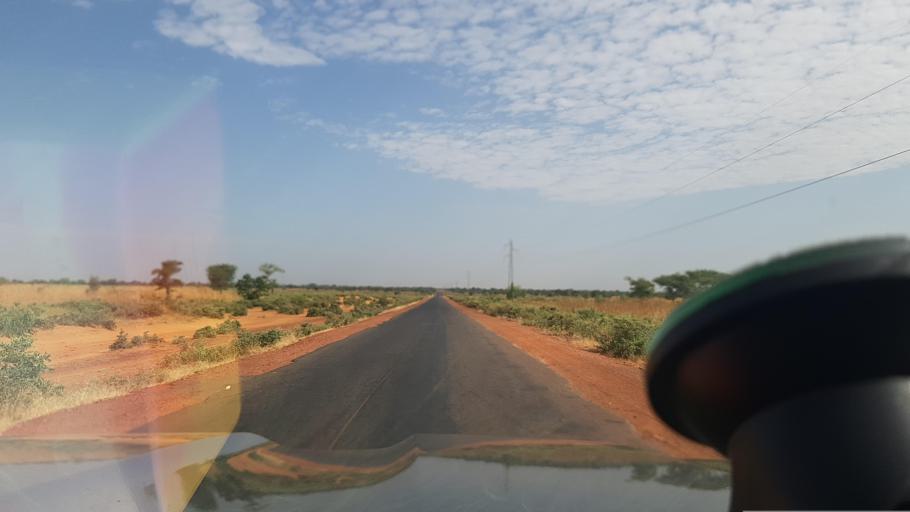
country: ML
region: Segou
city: Segou
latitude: 13.5456
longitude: -6.1196
